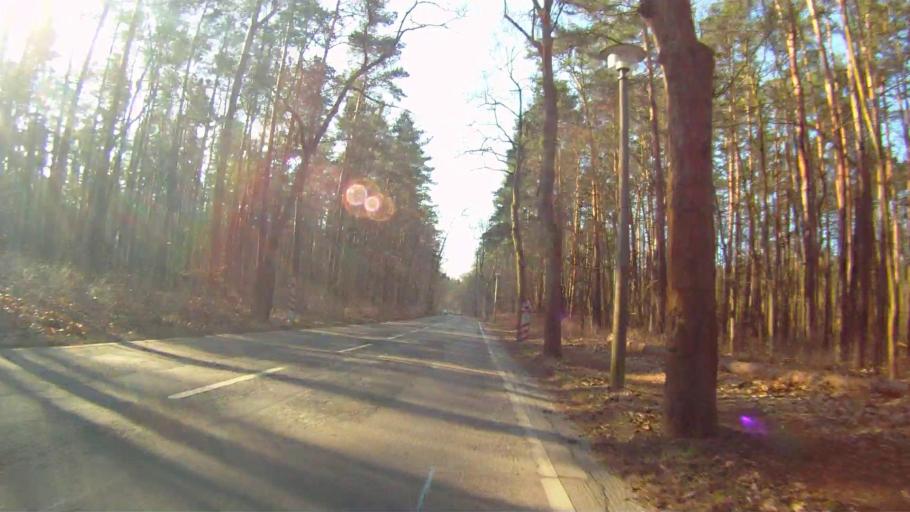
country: DE
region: Berlin
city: Rahnsdorf
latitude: 52.4536
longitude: 13.6995
